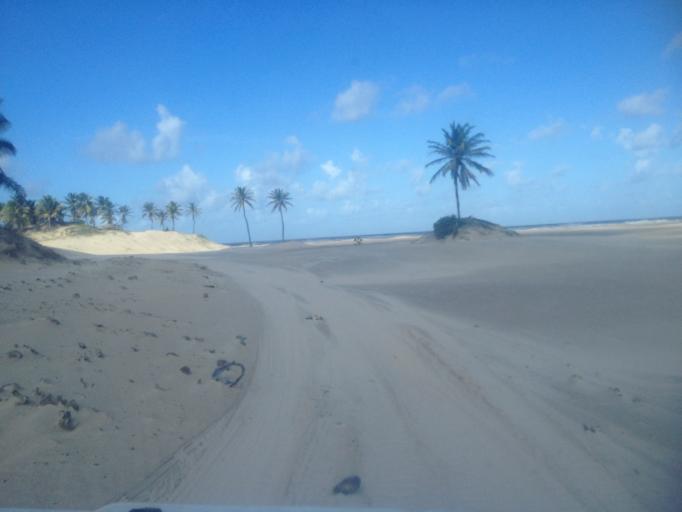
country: BR
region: Sergipe
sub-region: Indiaroba
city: Indiaroba
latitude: -11.4761
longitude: -37.3665
